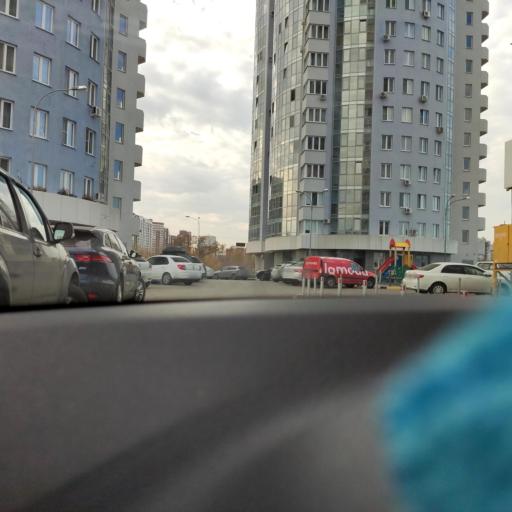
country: RU
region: Samara
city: Samara
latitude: 53.2220
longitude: 50.1694
